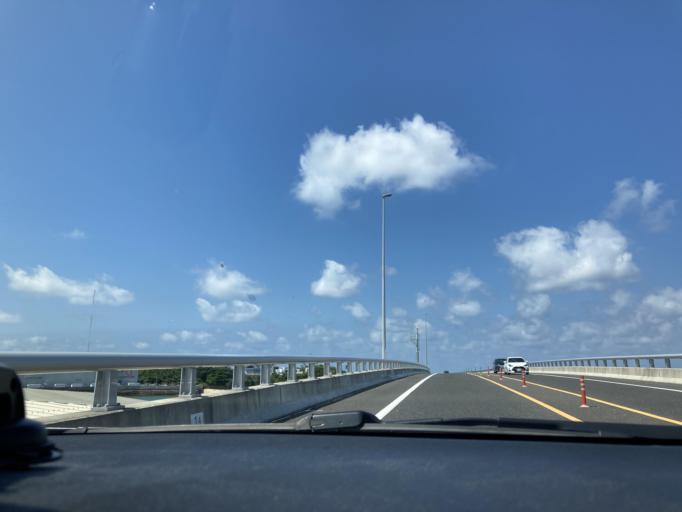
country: JP
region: Okinawa
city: Ginowan
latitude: 26.2738
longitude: 127.7115
